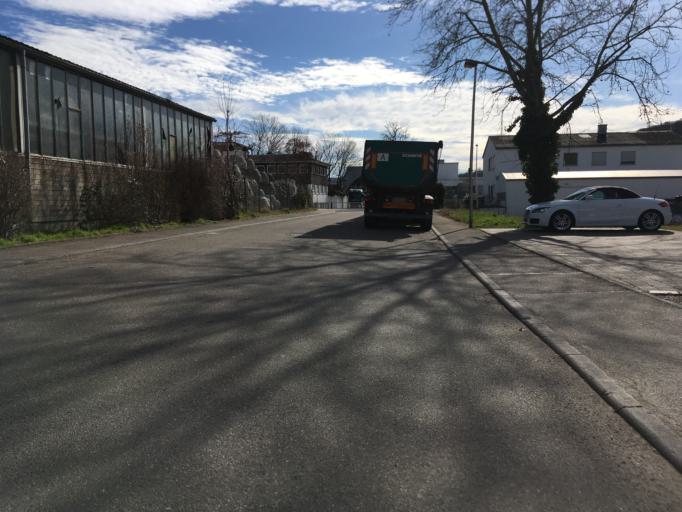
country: DE
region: Baden-Wuerttemberg
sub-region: Regierungsbezirk Stuttgart
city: Mundelsheim
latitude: 48.9962
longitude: 9.2057
